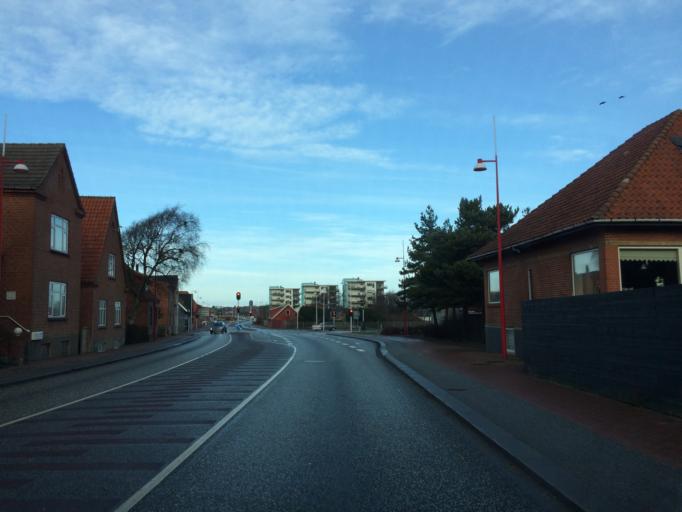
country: DK
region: Central Jutland
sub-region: Struer Kommune
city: Struer
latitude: 56.4923
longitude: 8.5839
